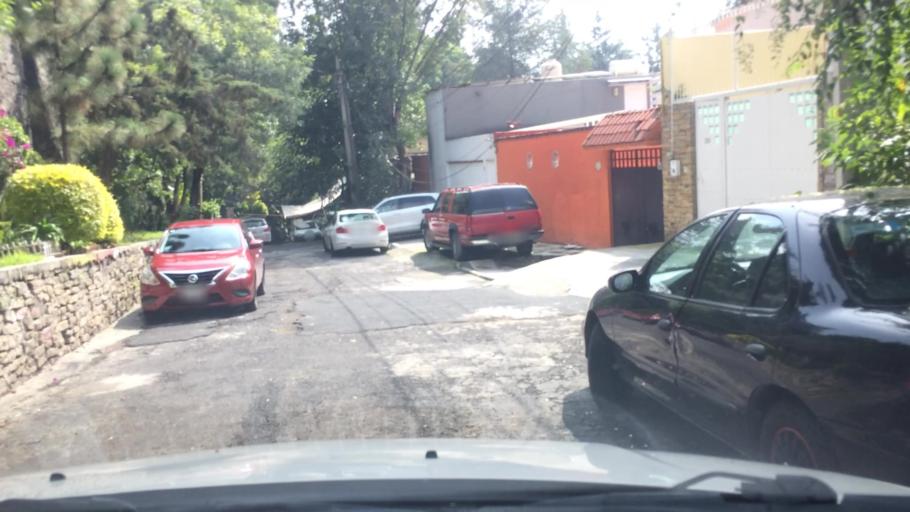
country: MX
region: Mexico City
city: Alvaro Obregon
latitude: 19.3491
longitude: -99.2164
